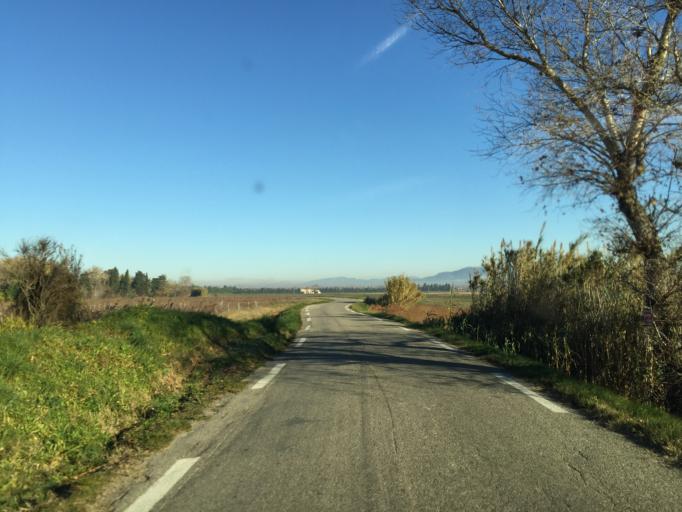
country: FR
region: Provence-Alpes-Cote d'Azur
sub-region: Departement du Vaucluse
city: Bedarrides
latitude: 44.0434
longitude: 4.9314
